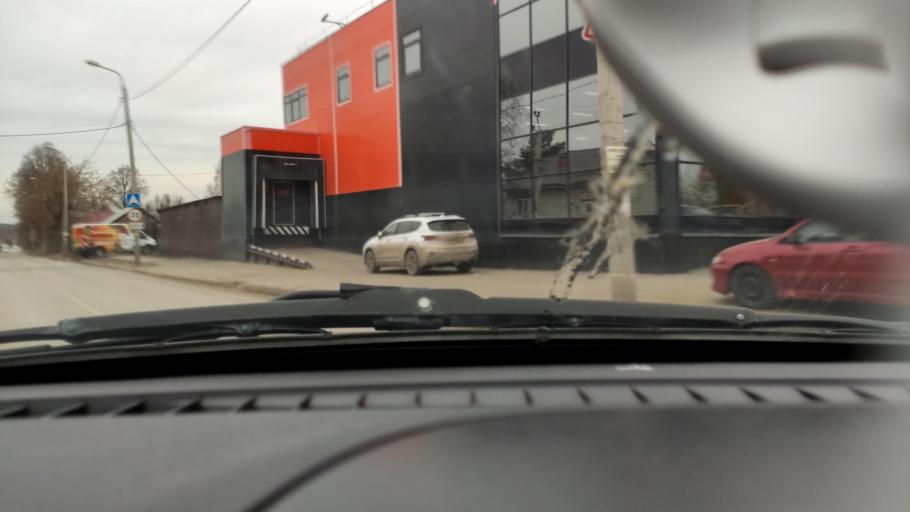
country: RU
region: Perm
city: Perm
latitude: 58.0257
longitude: 56.3333
